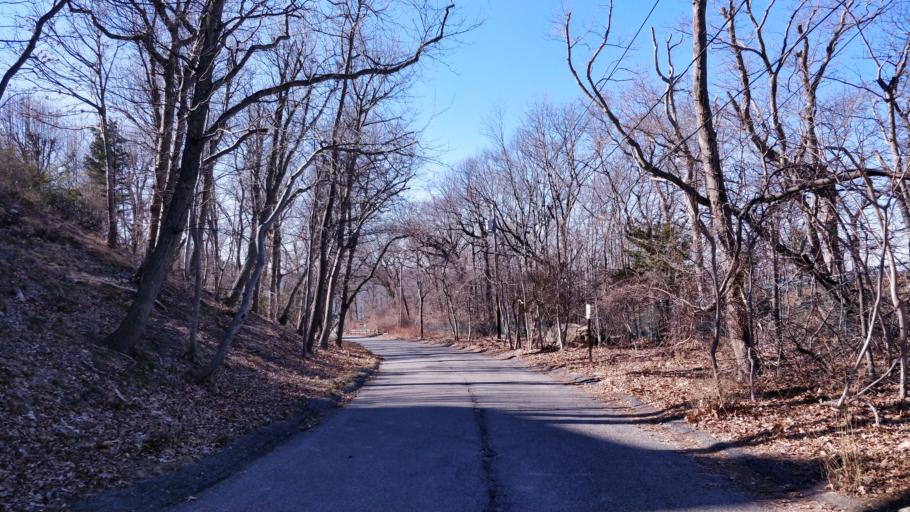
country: US
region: New York
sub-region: Suffolk County
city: Port Jefferson
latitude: 40.9676
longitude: -73.0754
